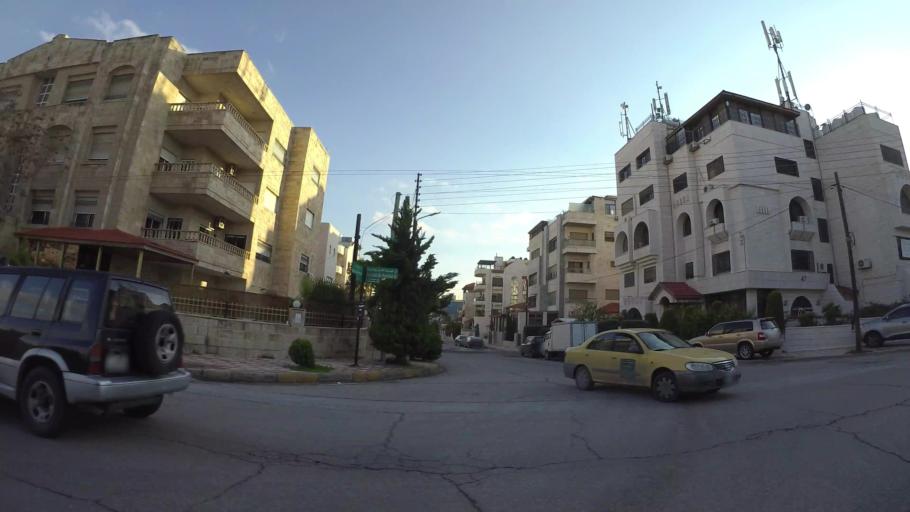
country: JO
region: Amman
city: Al Jubayhah
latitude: 31.9741
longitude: 35.8766
